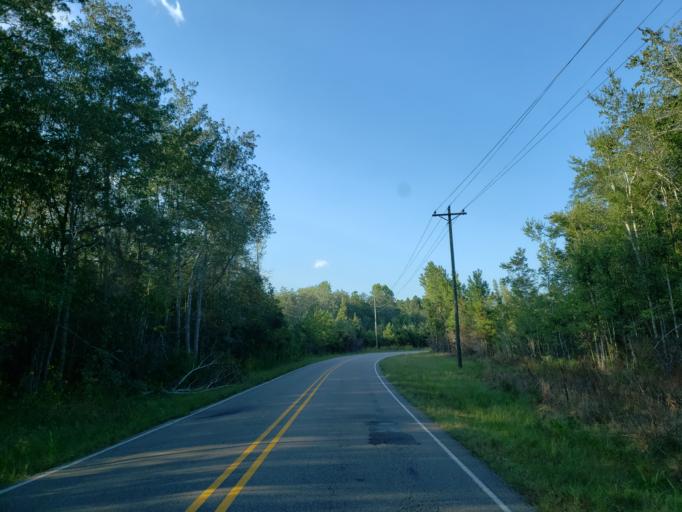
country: US
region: Mississippi
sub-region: Lamar County
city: West Hattiesburg
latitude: 31.2929
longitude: -89.4490
